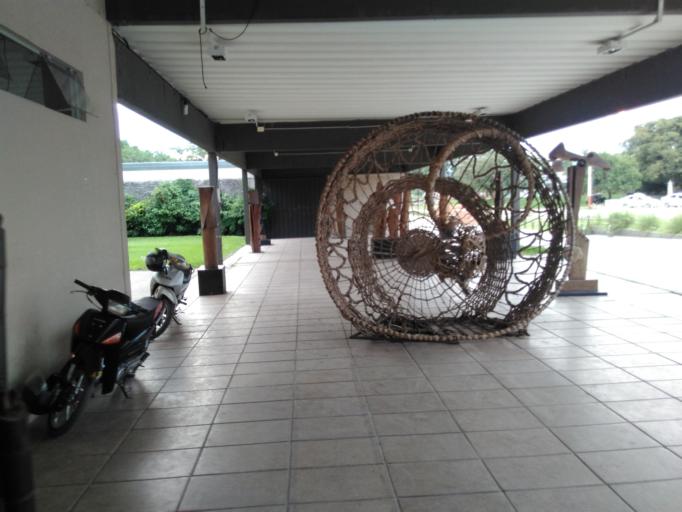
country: AR
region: Chaco
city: Resistencia
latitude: -27.4372
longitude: -58.9813
